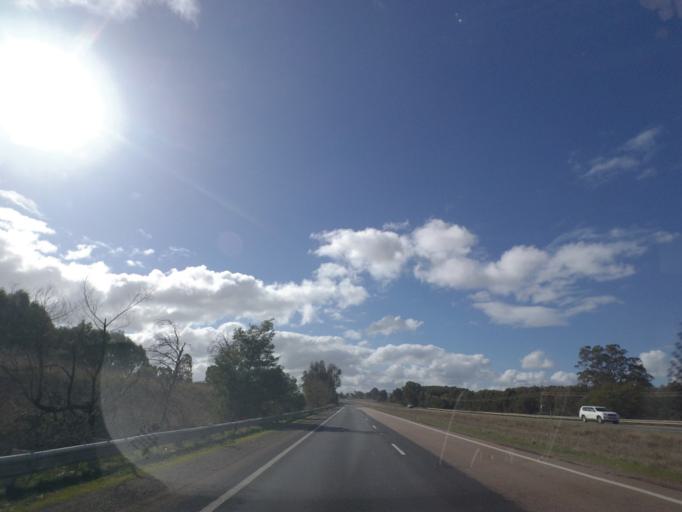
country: AU
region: New South Wales
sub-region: Albury Municipality
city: Lavington
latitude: -35.9770
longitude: 147.0018
